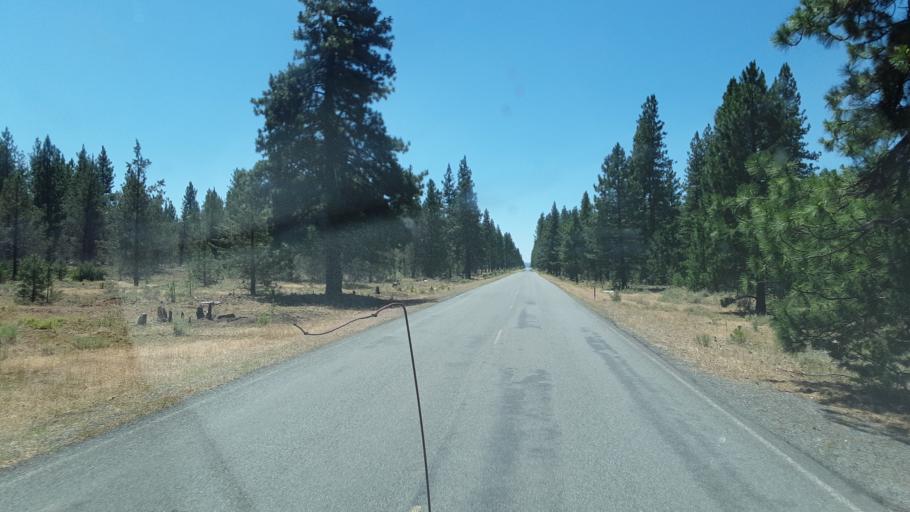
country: US
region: California
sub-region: Siskiyou County
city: Tulelake
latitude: 41.4110
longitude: -121.1788
